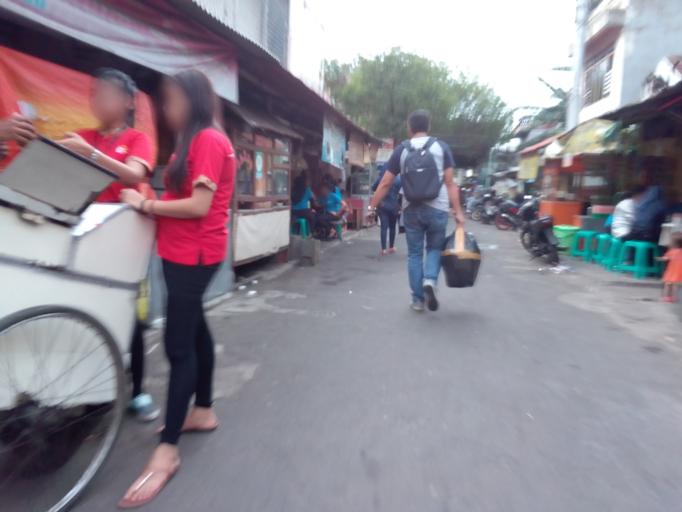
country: ID
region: Jakarta Raya
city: Jakarta
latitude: -6.1660
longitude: 106.8030
